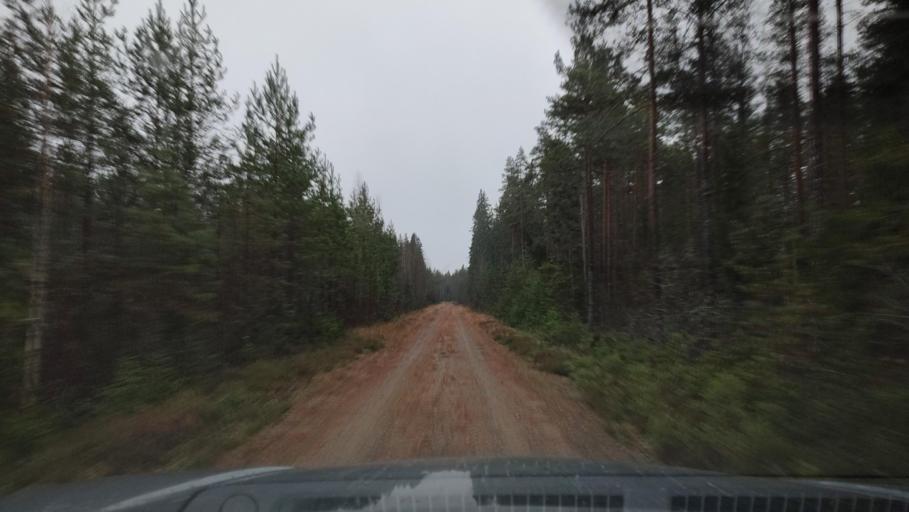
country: FI
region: Southern Ostrobothnia
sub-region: Suupohja
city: Karijoki
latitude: 62.1488
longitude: 21.5914
